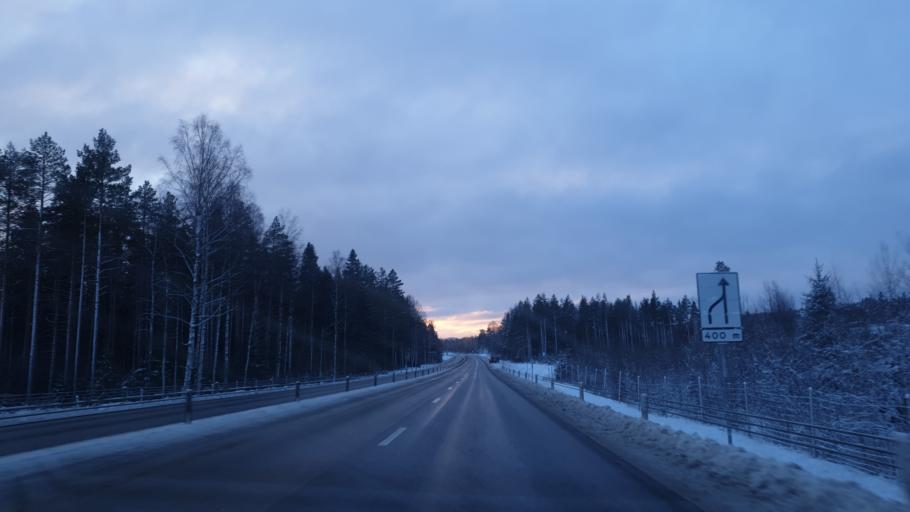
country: SE
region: Vaesternorrland
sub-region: OErnskoeldsviks Kommun
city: Husum
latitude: 63.4851
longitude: 19.3044
